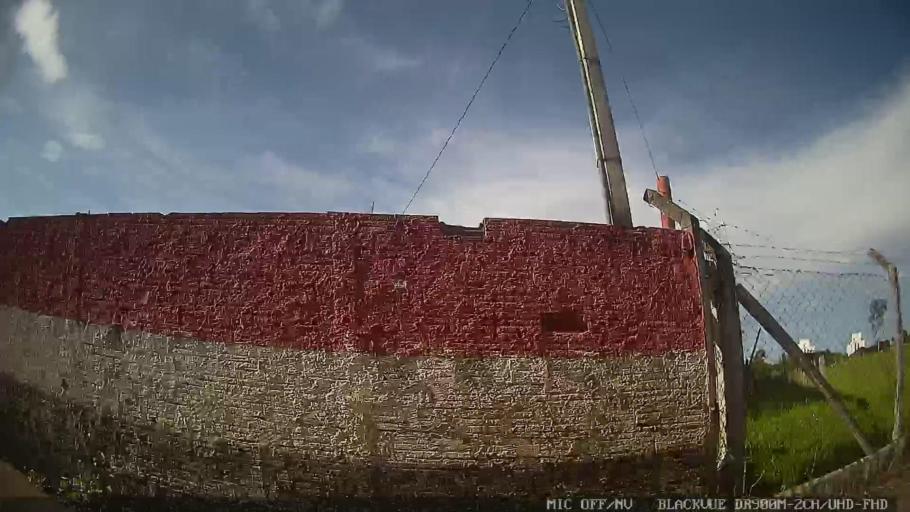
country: BR
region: Sao Paulo
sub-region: Tiete
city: Tiete
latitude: -23.0942
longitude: -47.7052
